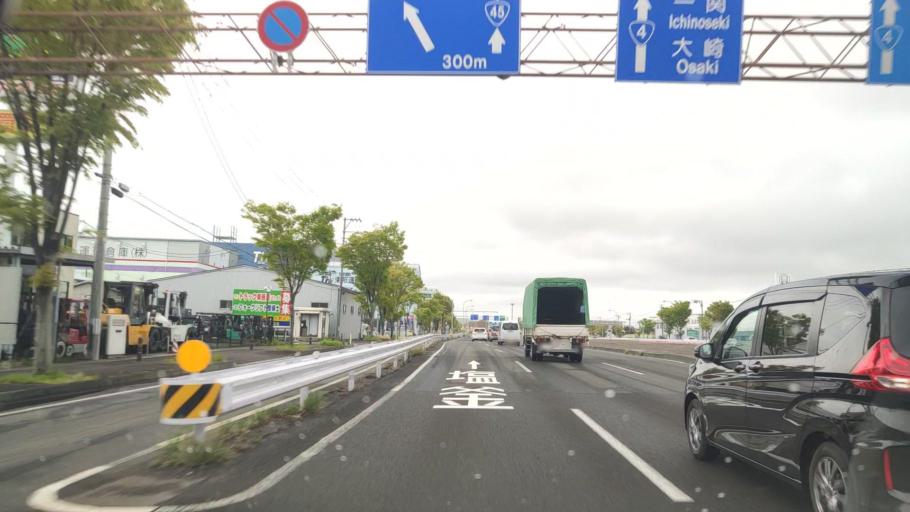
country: JP
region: Miyagi
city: Sendai-shi
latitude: 38.2615
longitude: 140.9378
